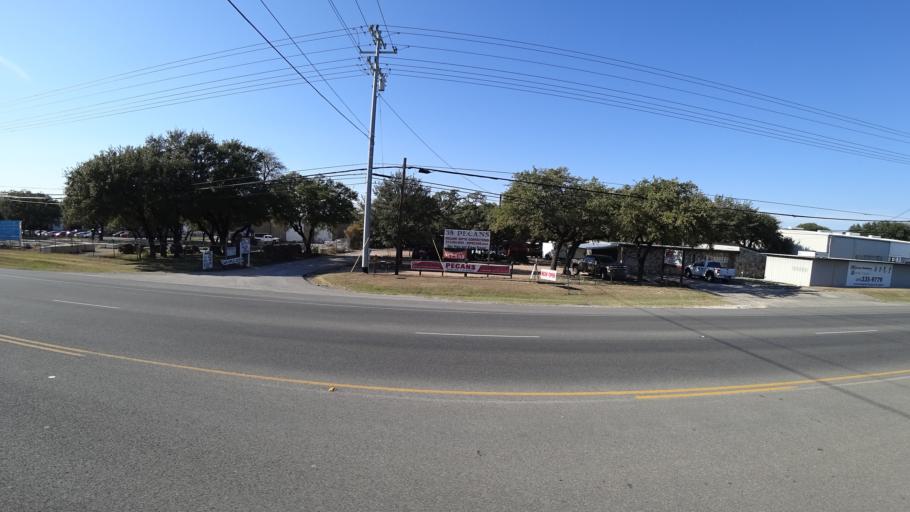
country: US
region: Texas
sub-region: Williamson County
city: Anderson Mill
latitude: 30.4420
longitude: -97.8339
